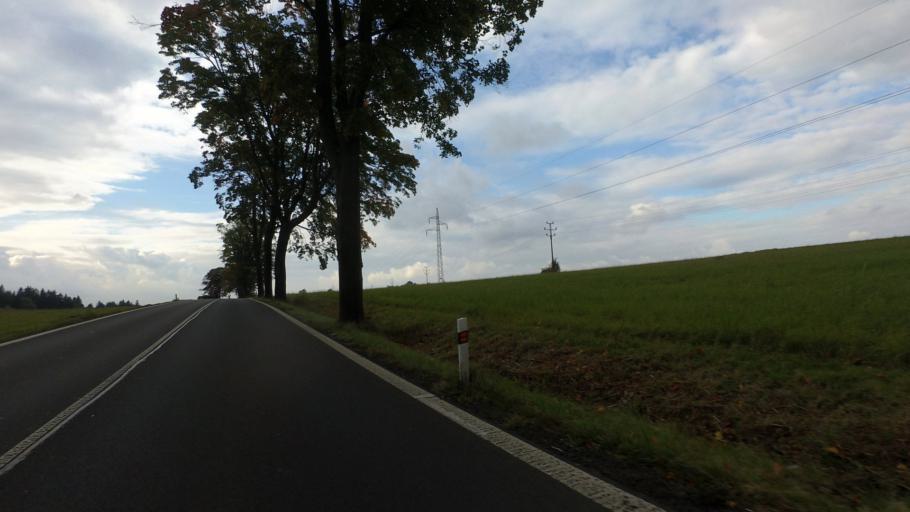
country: CZ
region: Ustecky
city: Stare Krecany
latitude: 50.9852
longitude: 14.5011
